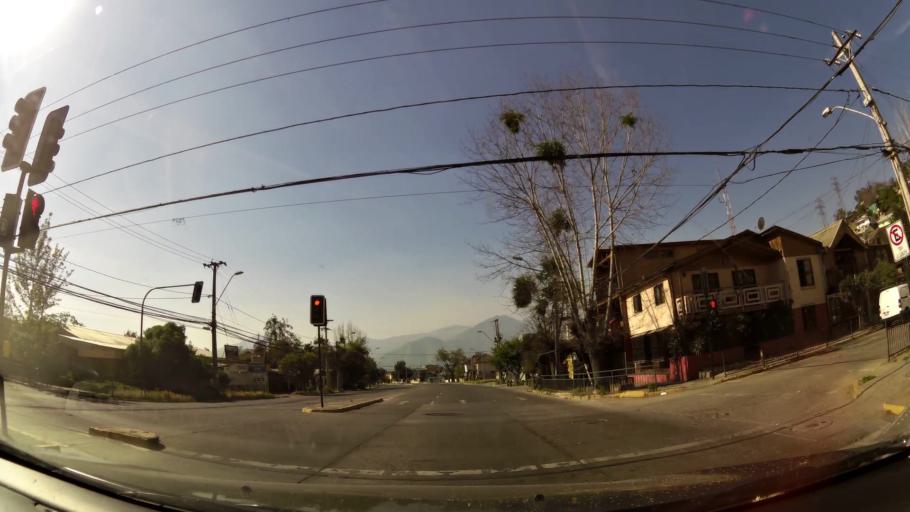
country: CL
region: Santiago Metropolitan
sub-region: Provincia de Santiago
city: Santiago
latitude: -33.4176
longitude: -70.6391
